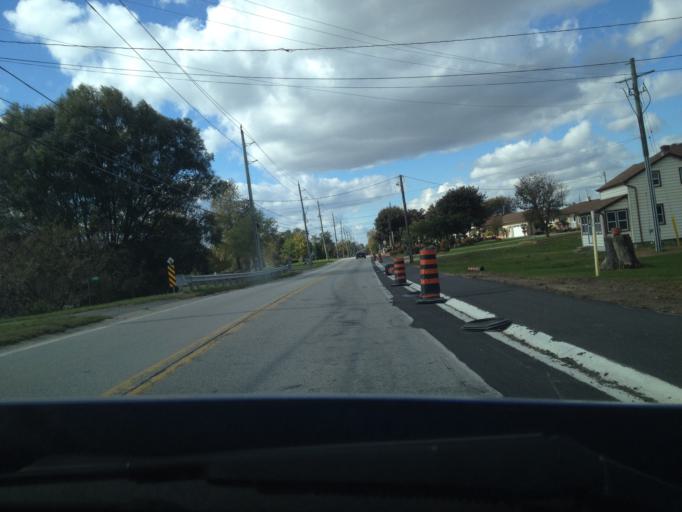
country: CA
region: Ontario
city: Amherstburg
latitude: 42.0352
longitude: -82.6305
